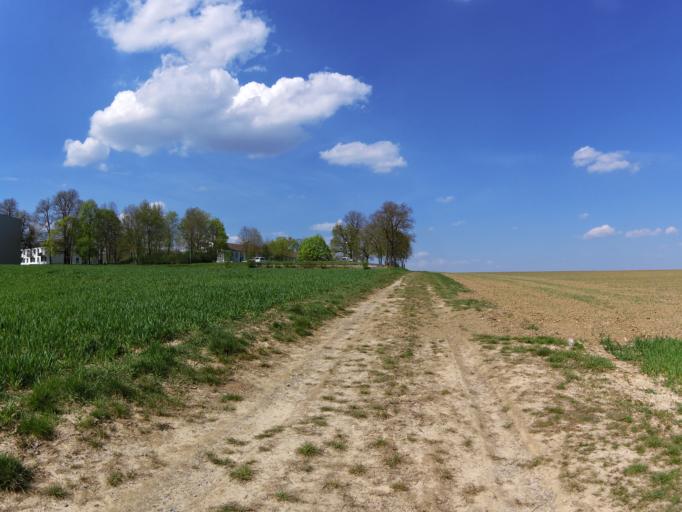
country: DE
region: Bavaria
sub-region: Regierungsbezirk Unterfranken
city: Giebelstadt
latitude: 49.6870
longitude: 9.9543
